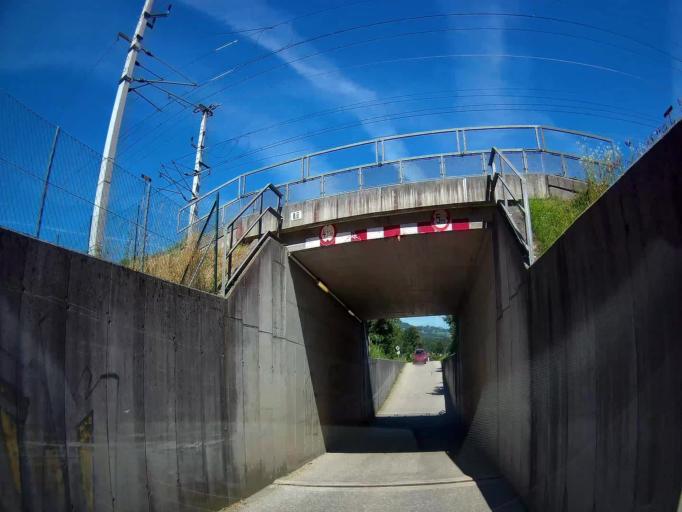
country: AT
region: Carinthia
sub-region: Politischer Bezirk Klagenfurt Land
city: Maria Saal
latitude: 46.6894
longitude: 14.3503
